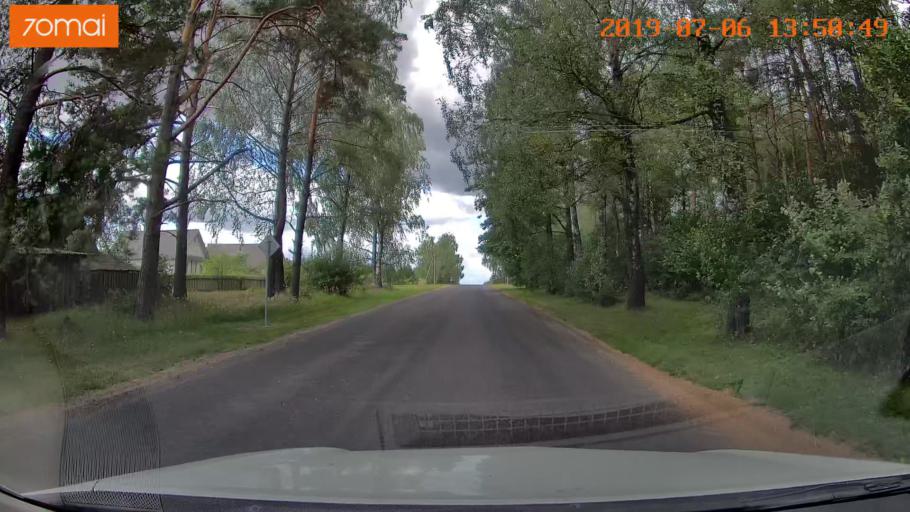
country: BY
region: Minsk
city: Ivyanyets
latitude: 53.7026
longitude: 26.8395
